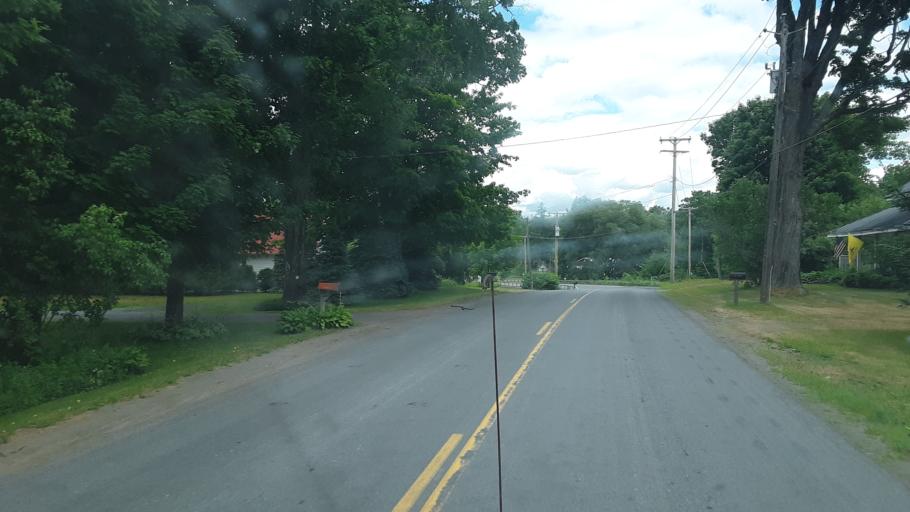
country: US
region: New York
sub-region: Oneida County
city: Rome
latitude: 43.3799
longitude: -75.5480
